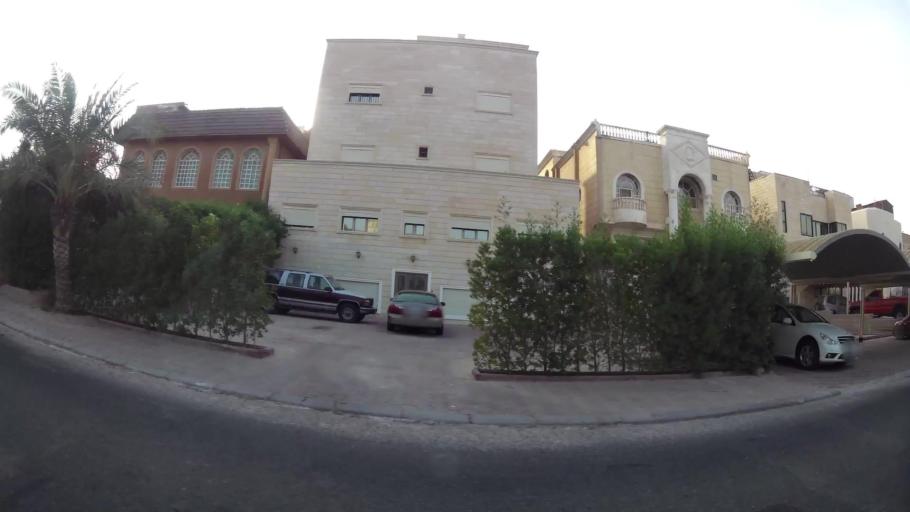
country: KW
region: Mubarak al Kabir
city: Mubarak al Kabir
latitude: 29.1885
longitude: 48.0711
